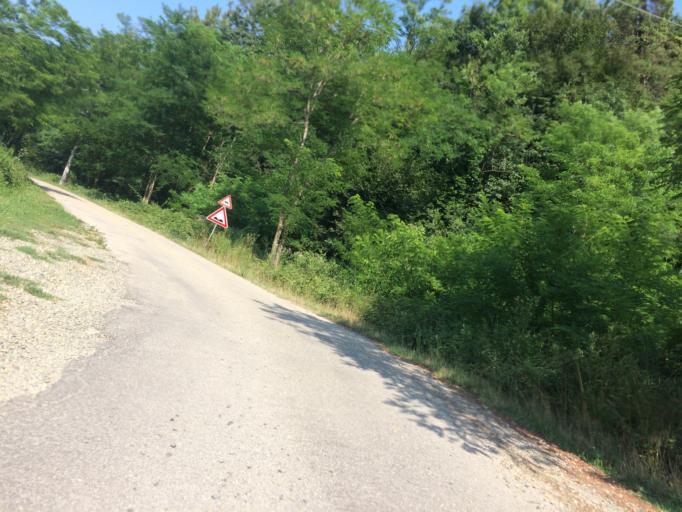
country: IT
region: Piedmont
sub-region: Provincia di Cuneo
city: Cortemilia
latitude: 44.5687
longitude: 8.2052
